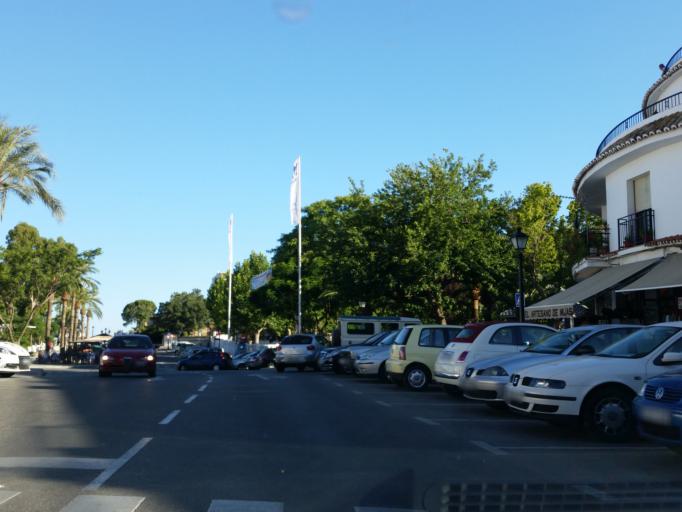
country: ES
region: Andalusia
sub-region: Provincia de Malaga
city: Mijas
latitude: 36.5966
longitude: -4.6371
